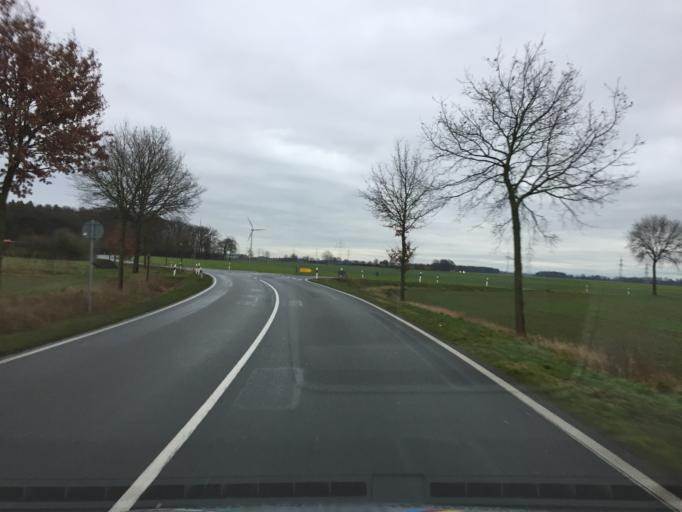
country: DE
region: Lower Saxony
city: Steyerberg
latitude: 52.5607
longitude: 9.0287
